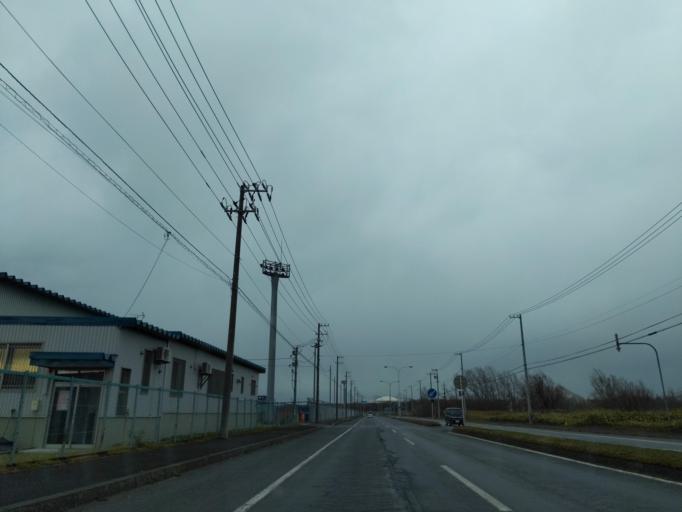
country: JP
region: Hokkaido
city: Ishikari
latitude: 43.1901
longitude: 141.2952
